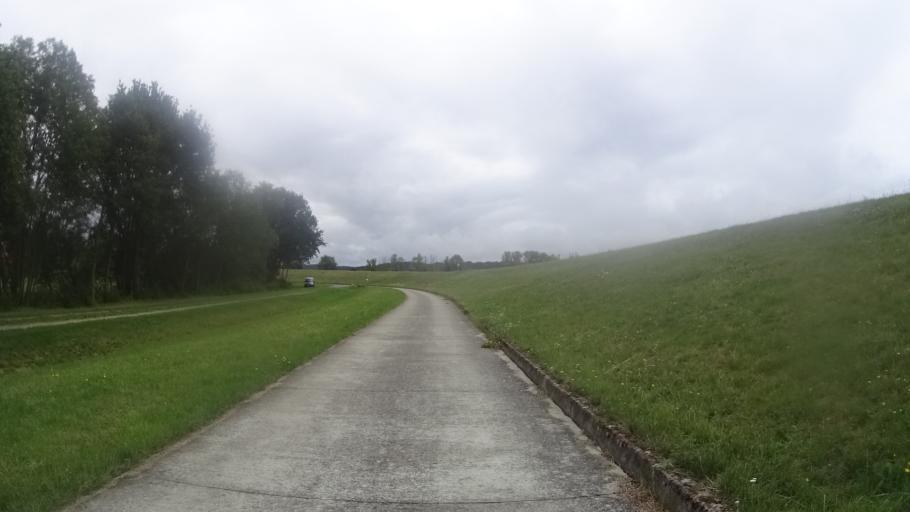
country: DE
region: Lower Saxony
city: Tosterglope
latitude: 53.2603
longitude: 10.8312
